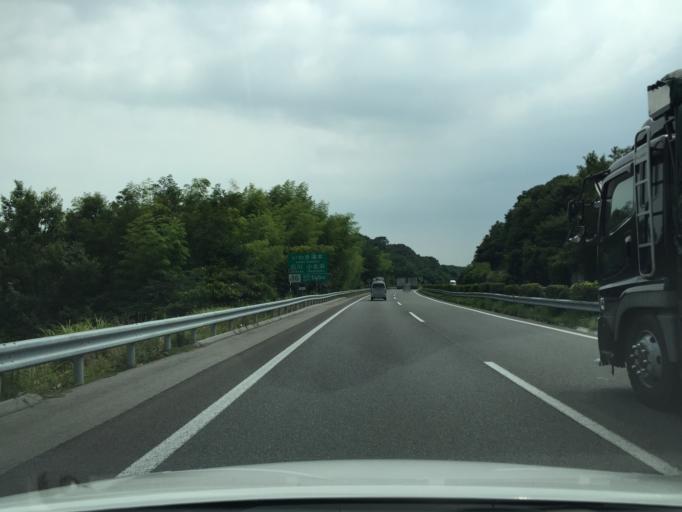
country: JP
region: Fukushima
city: Iwaki
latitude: 37.0106
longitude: 140.8142
